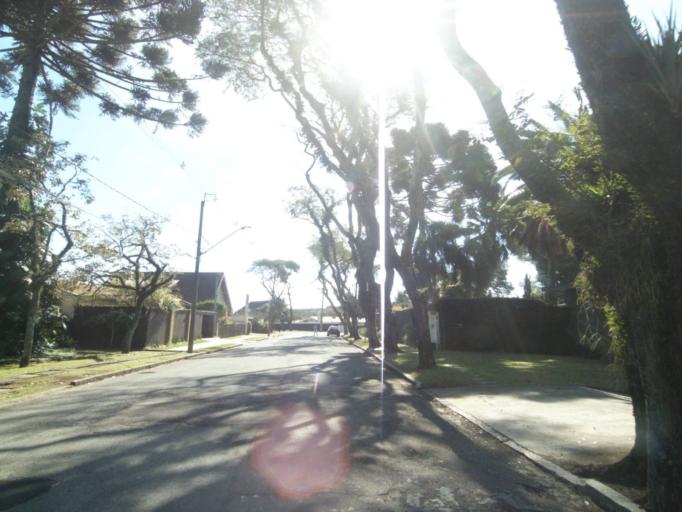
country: BR
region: Parana
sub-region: Curitiba
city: Curitiba
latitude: -25.4182
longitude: -49.2331
